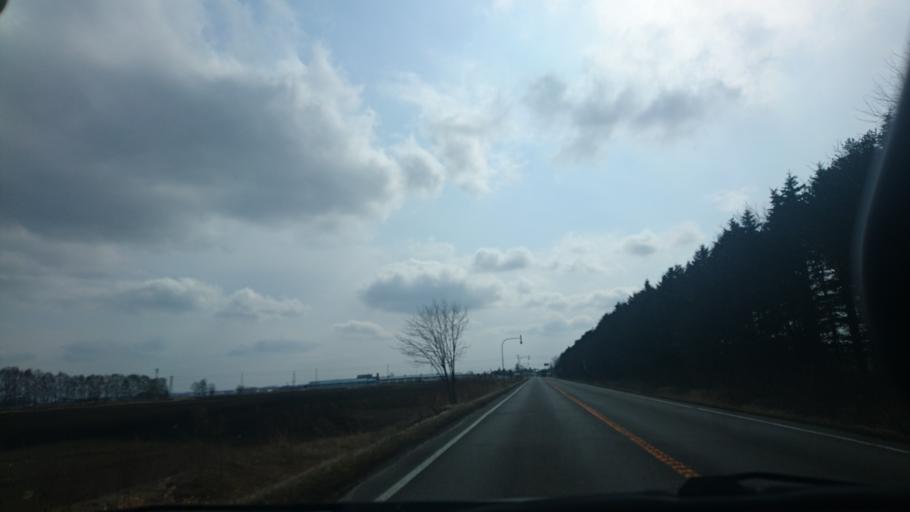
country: JP
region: Hokkaido
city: Otofuke
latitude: 43.1579
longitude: 143.2454
